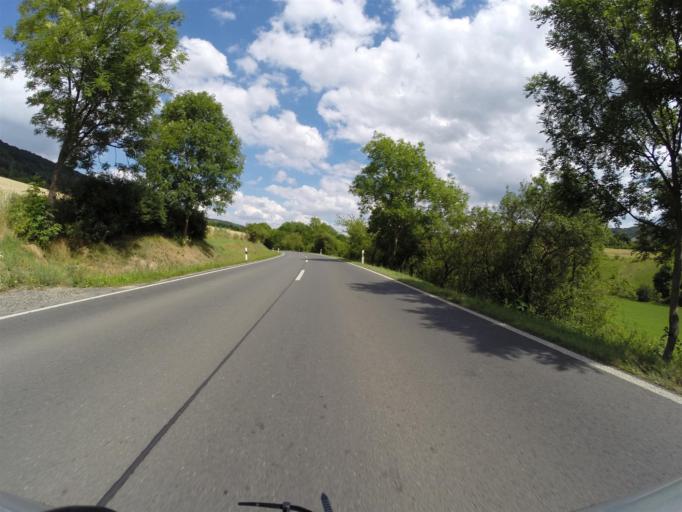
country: DE
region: Thuringia
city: Grosslobichau
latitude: 50.9327
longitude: 11.6473
